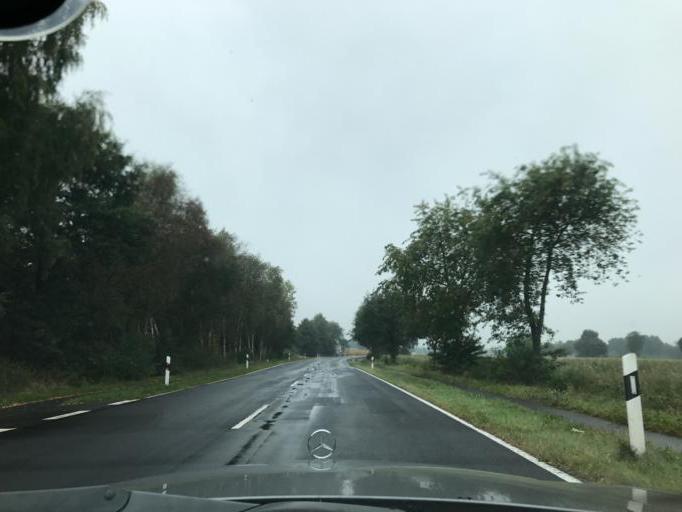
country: DE
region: Lower Saxony
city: Papenburg
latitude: 53.0786
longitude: 7.3509
